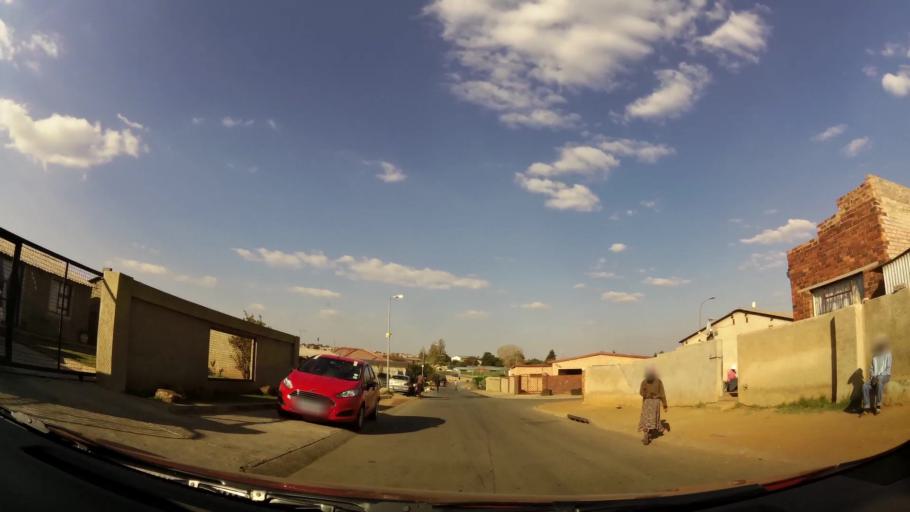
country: ZA
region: Gauteng
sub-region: City of Johannesburg Metropolitan Municipality
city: Soweto
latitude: -26.2168
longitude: 27.8761
